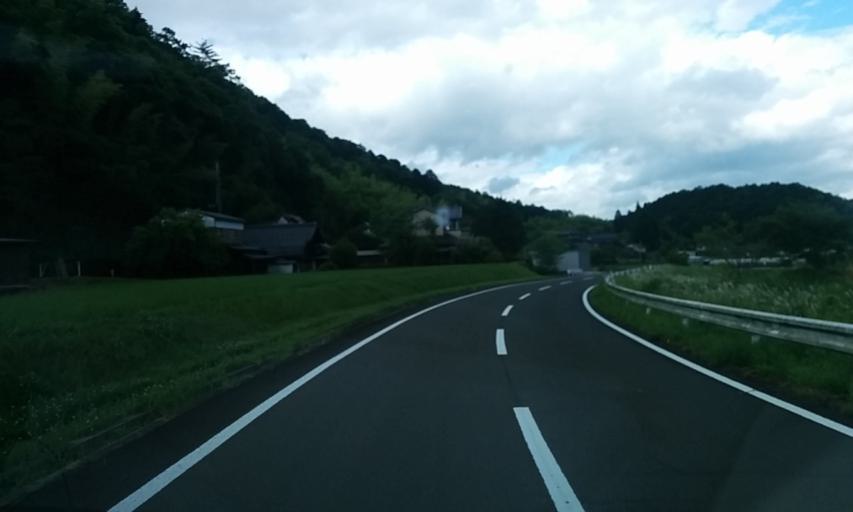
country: JP
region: Kyoto
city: Ayabe
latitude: 35.3790
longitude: 135.2172
